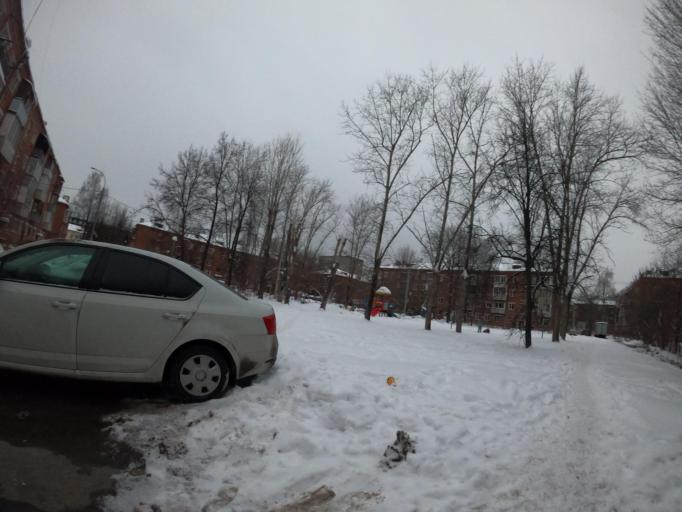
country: RU
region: Moskovskaya
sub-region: Podol'skiy Rayon
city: Podol'sk
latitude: 55.4157
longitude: 37.5337
